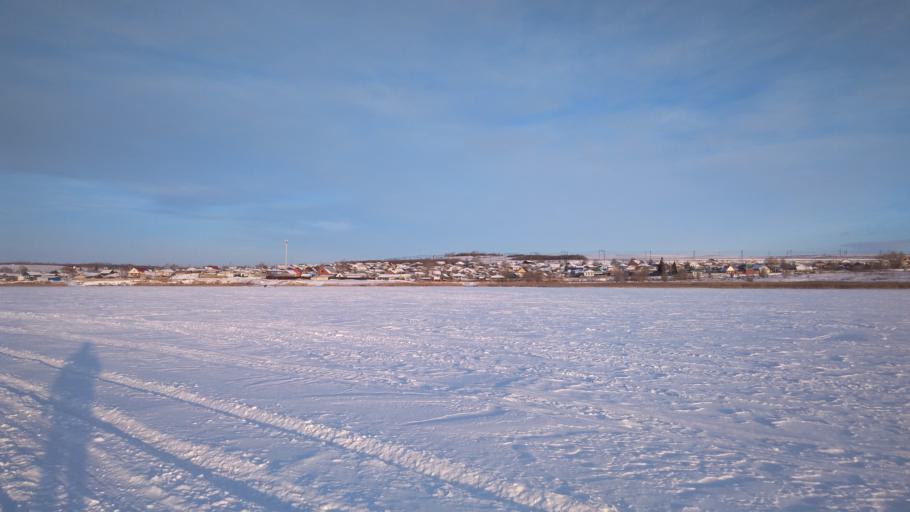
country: RU
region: Chelyabinsk
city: Troitsk
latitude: 54.0841
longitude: 61.5858
